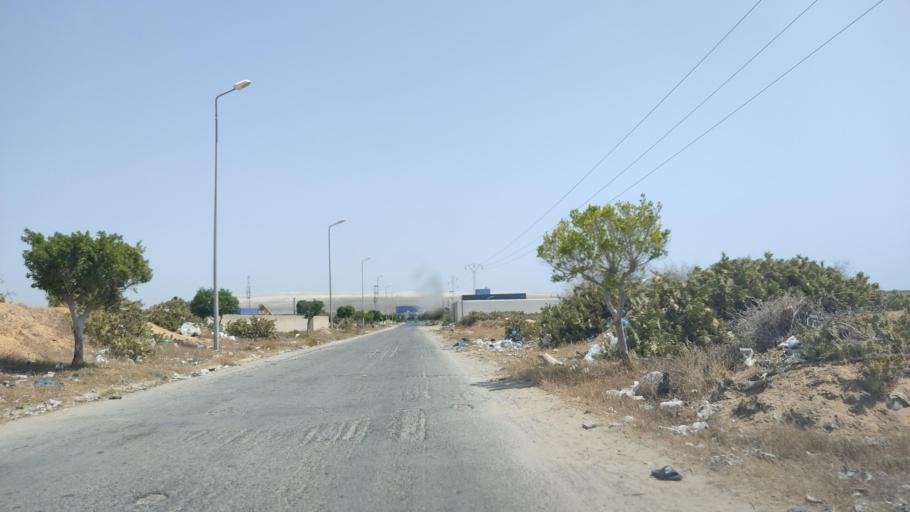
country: TN
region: Safaqis
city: Sfax
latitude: 34.6860
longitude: 10.7238
